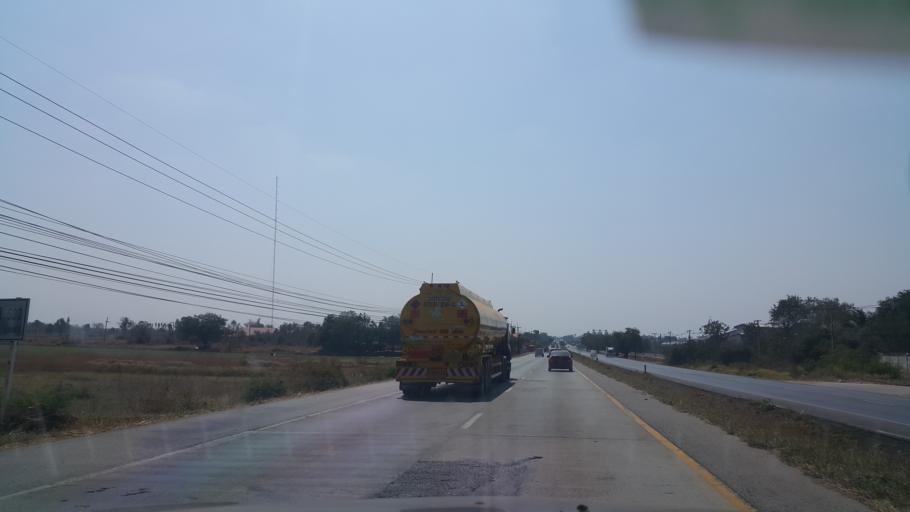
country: TH
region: Khon Kaen
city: Phon
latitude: 15.8647
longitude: 102.6284
